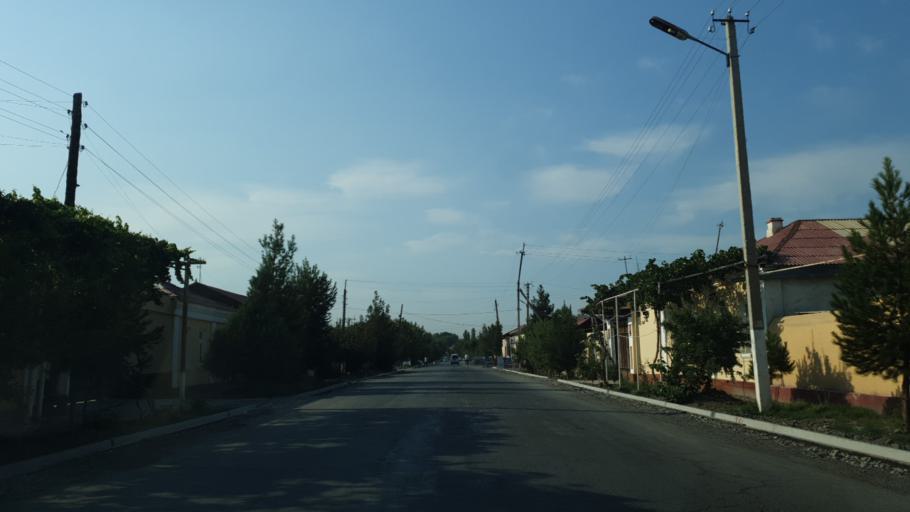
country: UZ
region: Fergana
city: Yaypan
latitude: 40.3725
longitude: 70.8130
